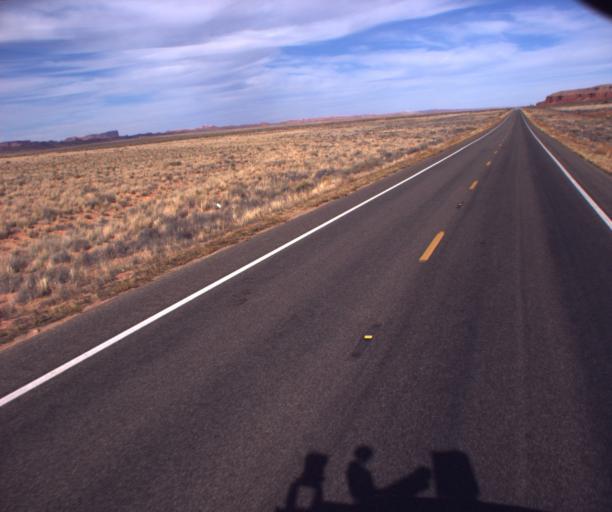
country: US
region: Arizona
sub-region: Navajo County
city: Kayenta
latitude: 36.7506
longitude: -110.0621
